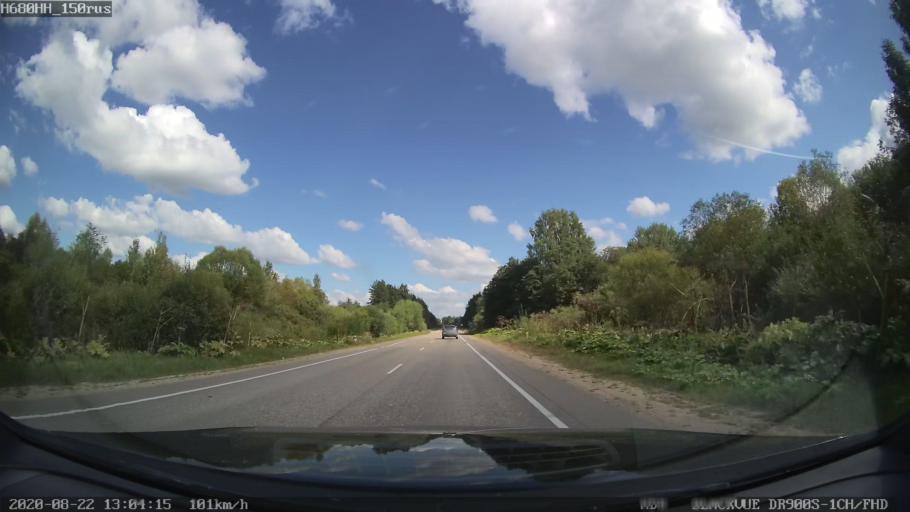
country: RU
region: Tverskaya
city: Bezhetsk
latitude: 57.6648
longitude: 36.4262
